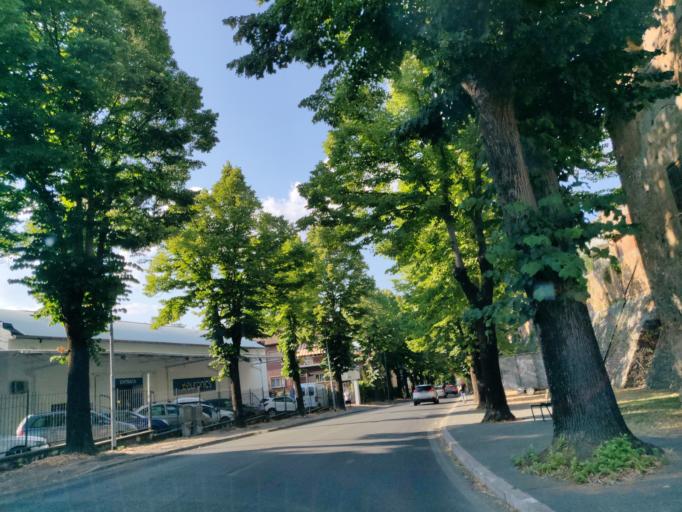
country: IT
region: Latium
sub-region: Provincia di Viterbo
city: Acquapendente
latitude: 42.7438
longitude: 11.8631
